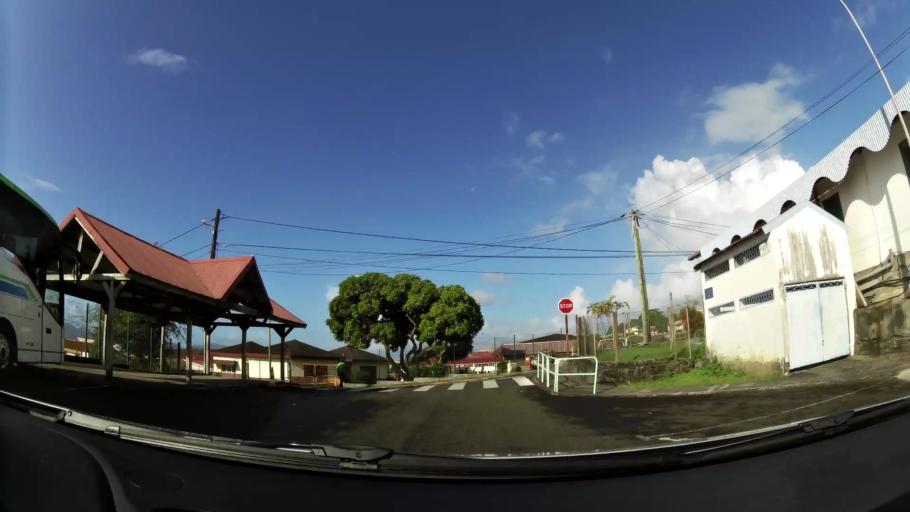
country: MQ
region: Martinique
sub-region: Martinique
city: Ducos
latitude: 14.5744
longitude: -60.9742
